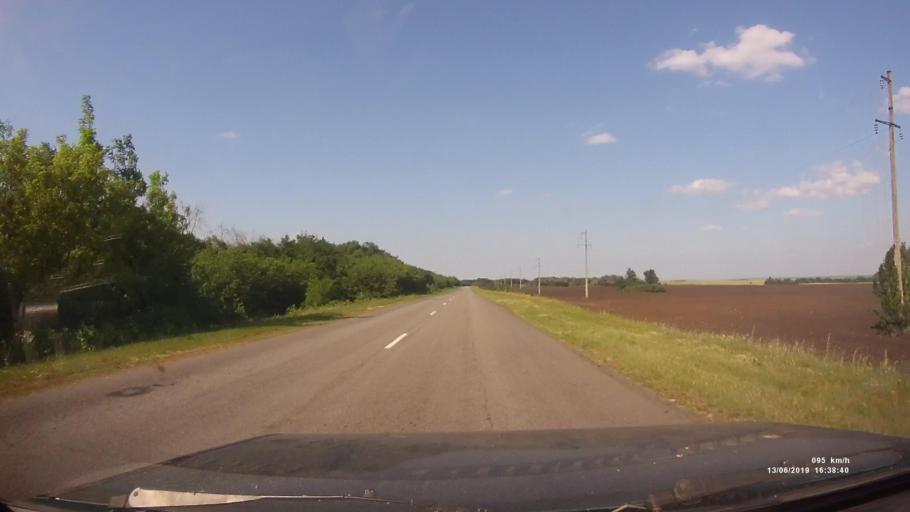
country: RU
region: Rostov
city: Kazanskaya
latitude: 49.9211
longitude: 41.3271
